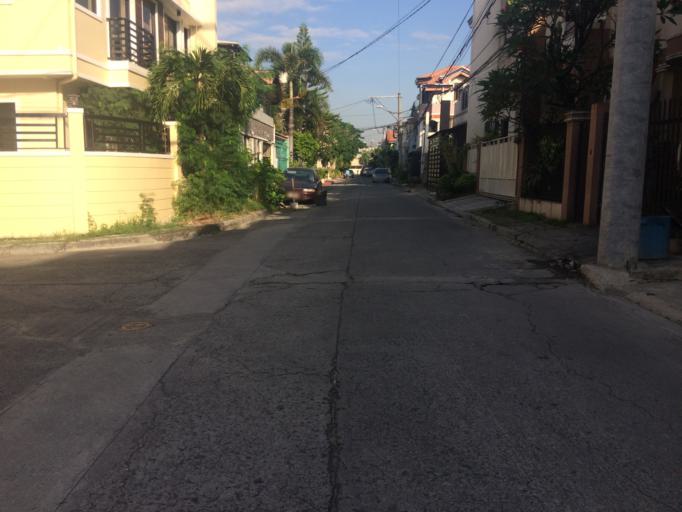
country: PH
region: Calabarzon
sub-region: Province of Rizal
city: Taytay
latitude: 14.5527
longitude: 121.1060
